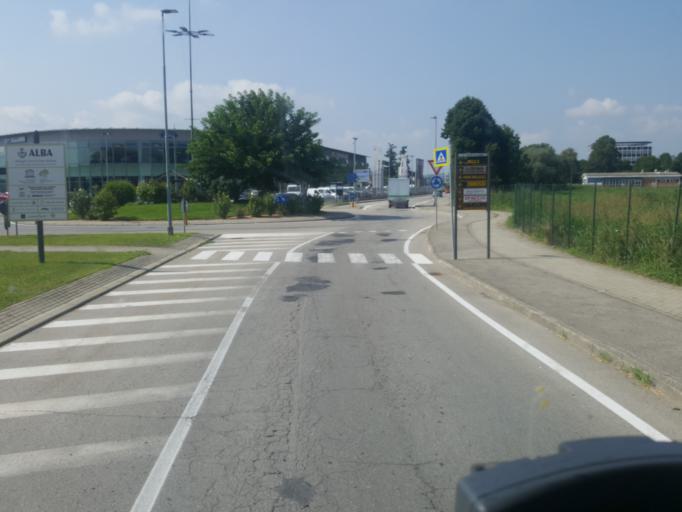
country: IT
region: Piedmont
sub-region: Provincia di Cuneo
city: Mussotto
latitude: 44.7213
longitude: 8.0374
